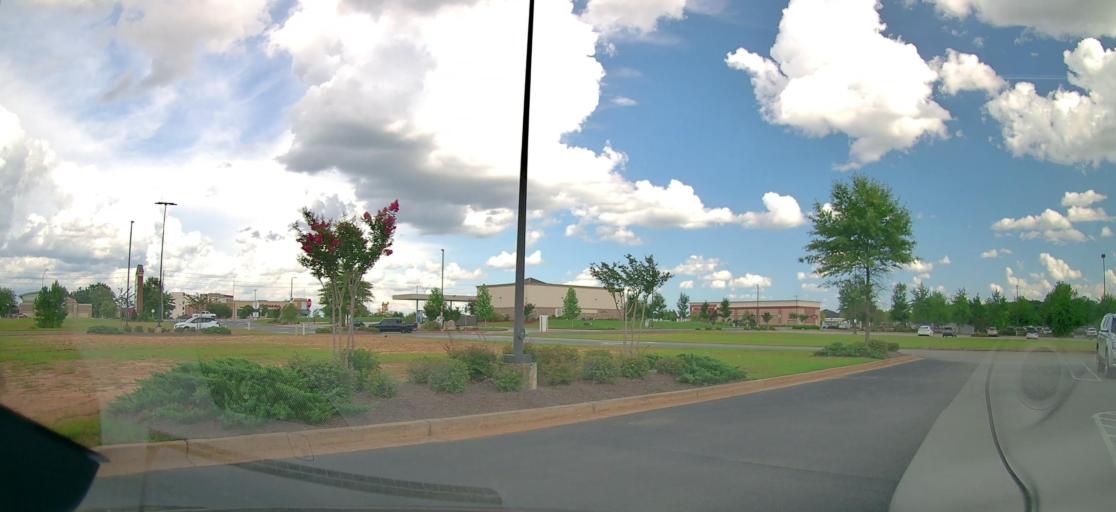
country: US
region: Georgia
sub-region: Houston County
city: Centerville
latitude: 32.5522
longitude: -83.6933
